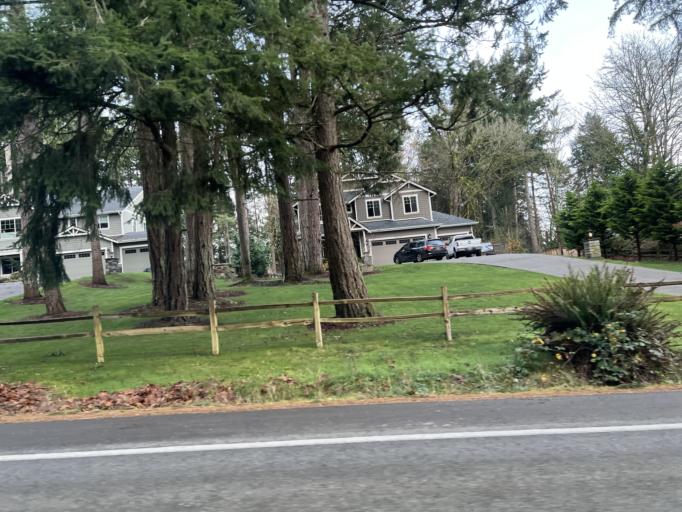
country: US
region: Washington
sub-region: Kitsap County
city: Bainbridge Island
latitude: 47.6596
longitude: -122.5188
